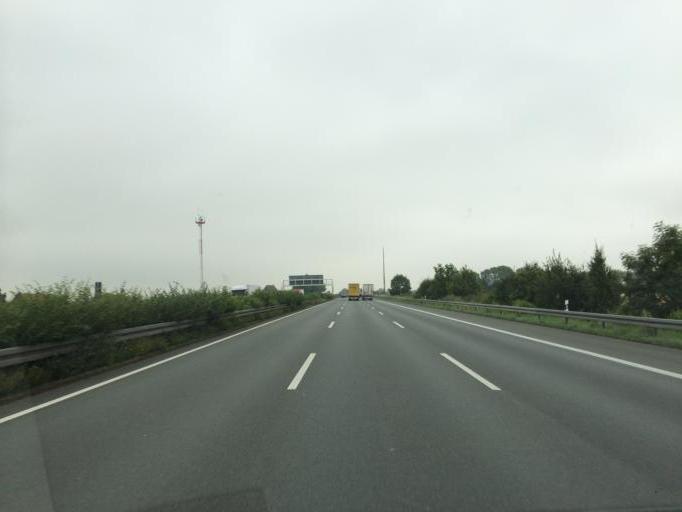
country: DE
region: North Rhine-Westphalia
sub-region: Regierungsbezirk Munster
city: Beckum
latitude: 51.7803
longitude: 8.0369
